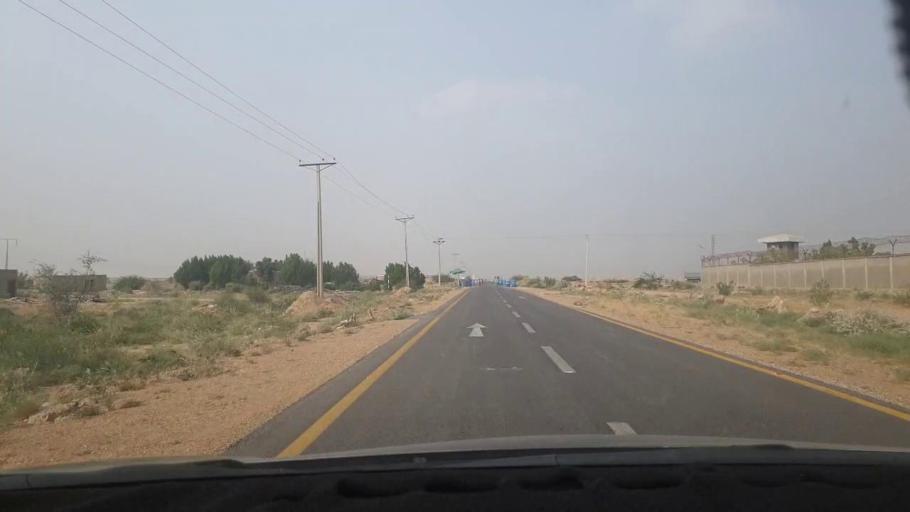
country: PK
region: Sindh
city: Jamshoro
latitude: 25.5642
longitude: 68.3174
